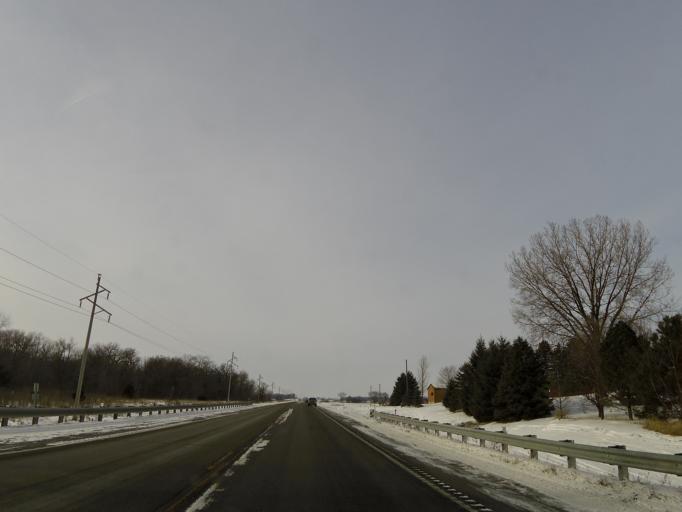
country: US
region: Minnesota
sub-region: Carver County
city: Mayer
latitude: 44.9057
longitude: -93.8978
